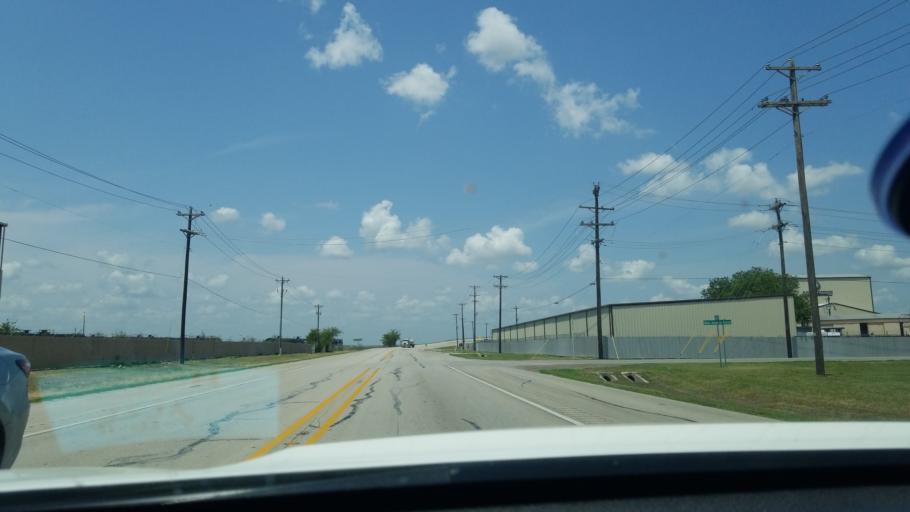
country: US
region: Texas
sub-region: Tarrant County
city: Eagle Mountain
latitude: 32.9388
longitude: -97.4196
